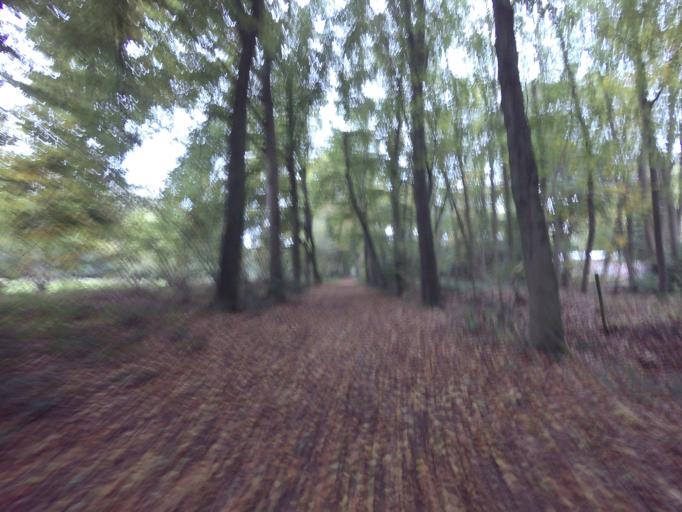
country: NL
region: North Brabant
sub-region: Gemeente Breda
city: Breda
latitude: 51.5483
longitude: 4.7831
